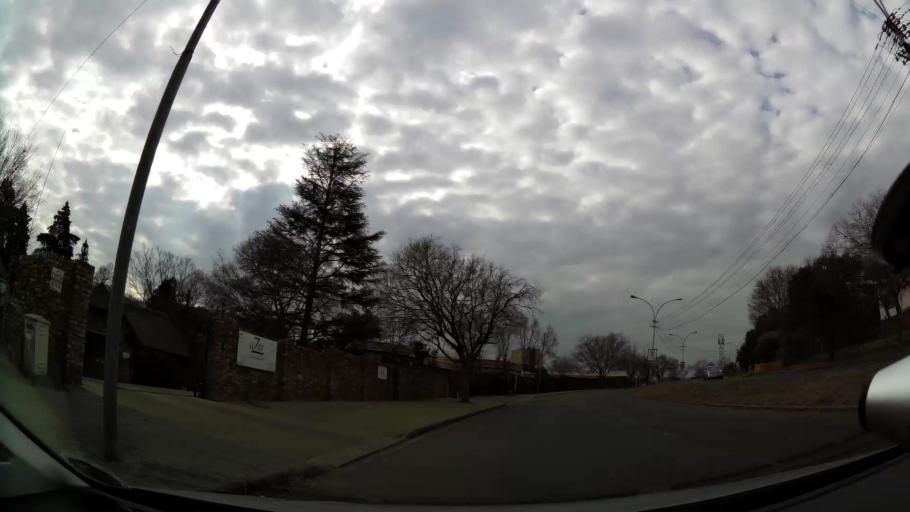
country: ZA
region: Orange Free State
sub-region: Mangaung Metropolitan Municipality
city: Bloemfontein
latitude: -29.0915
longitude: 26.2073
